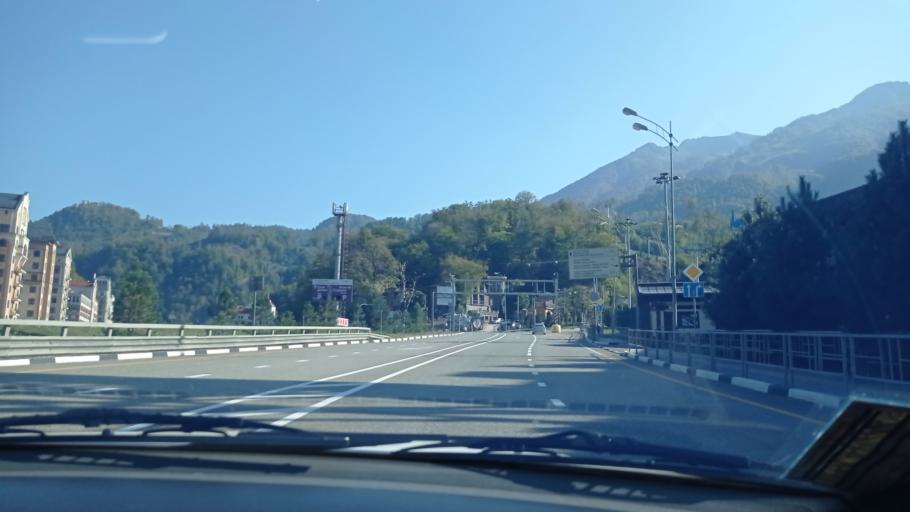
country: RU
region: Krasnodarskiy
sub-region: Sochi City
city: Krasnaya Polyana
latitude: 43.6766
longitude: 40.2843
